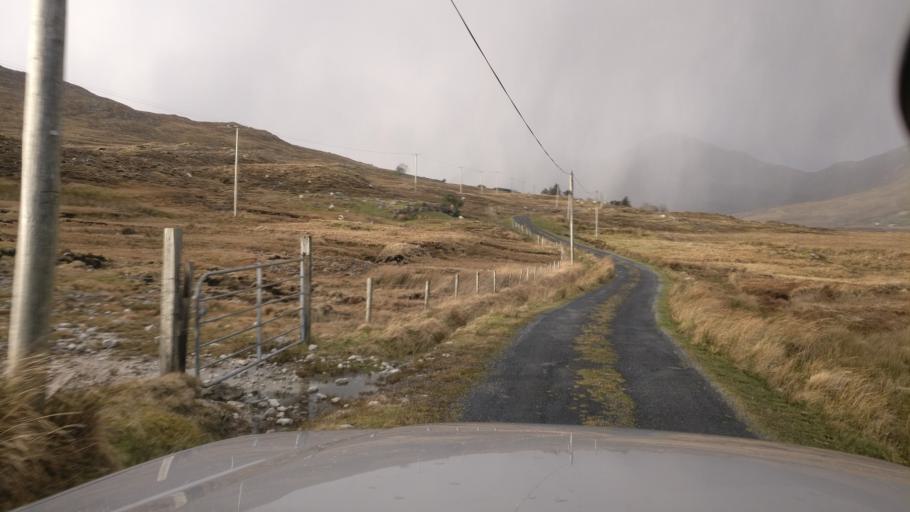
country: IE
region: Connaught
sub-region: County Galway
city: Clifden
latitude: 53.4818
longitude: -9.6961
